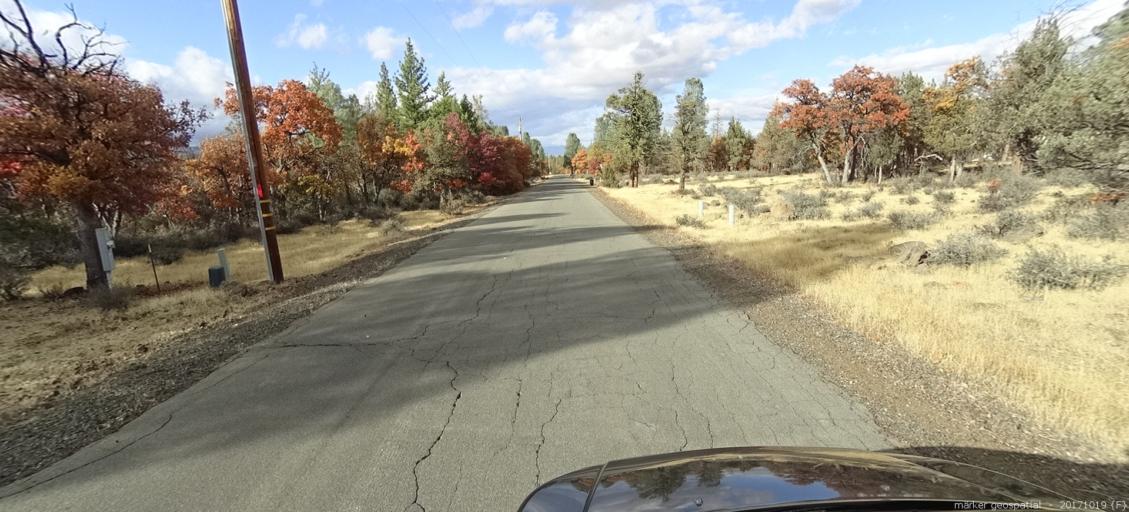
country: US
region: California
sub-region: Shasta County
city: Burney
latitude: 40.9665
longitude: -121.4408
